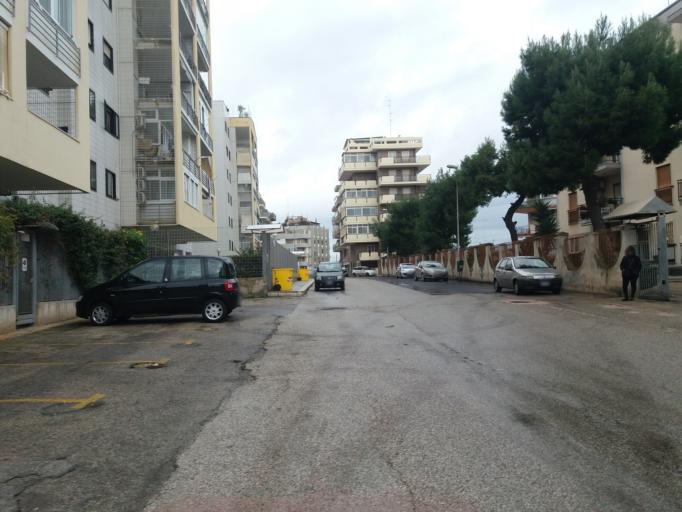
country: IT
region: Apulia
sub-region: Provincia di Bari
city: San Paolo
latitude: 41.1380
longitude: 16.8113
